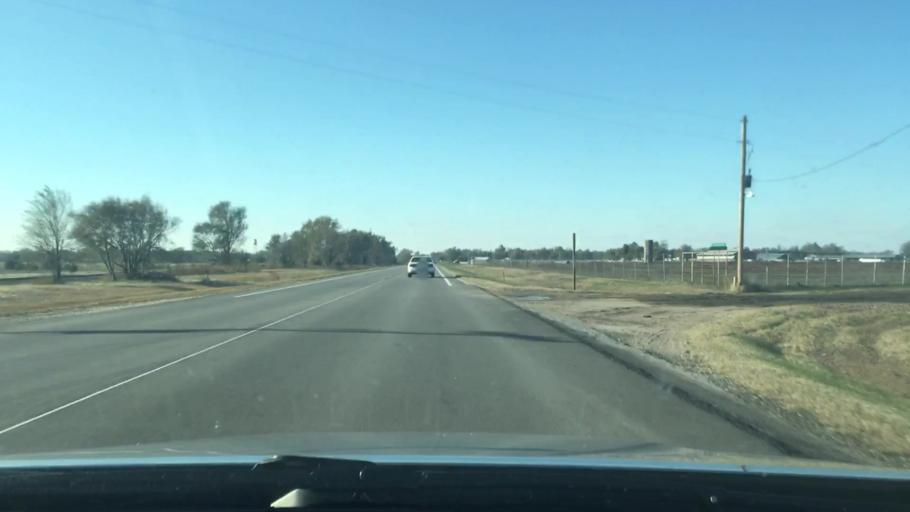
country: US
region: Kansas
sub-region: Reno County
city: Nickerson
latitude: 38.1372
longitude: -98.0687
